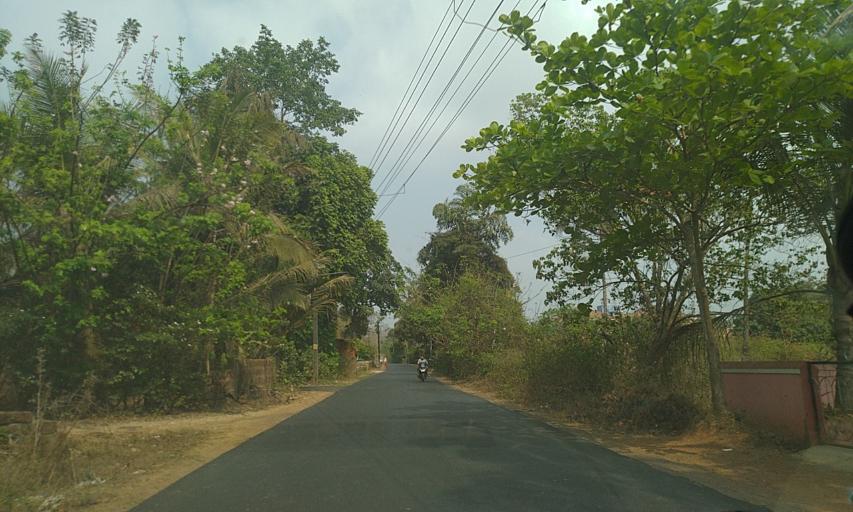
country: IN
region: Goa
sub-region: South Goa
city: Raia
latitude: 15.3080
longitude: 73.9621
